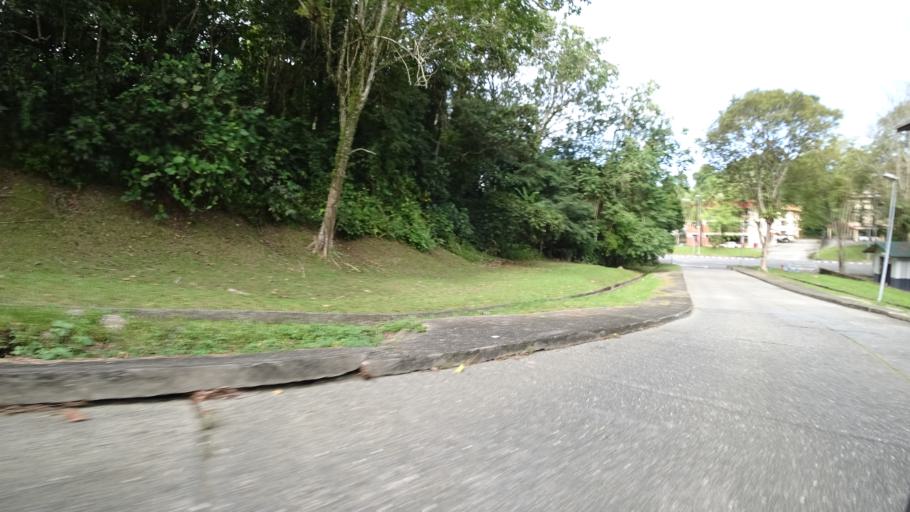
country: BN
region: Brunei and Muara
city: Bandar Seri Begawan
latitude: 4.8840
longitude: 114.9243
